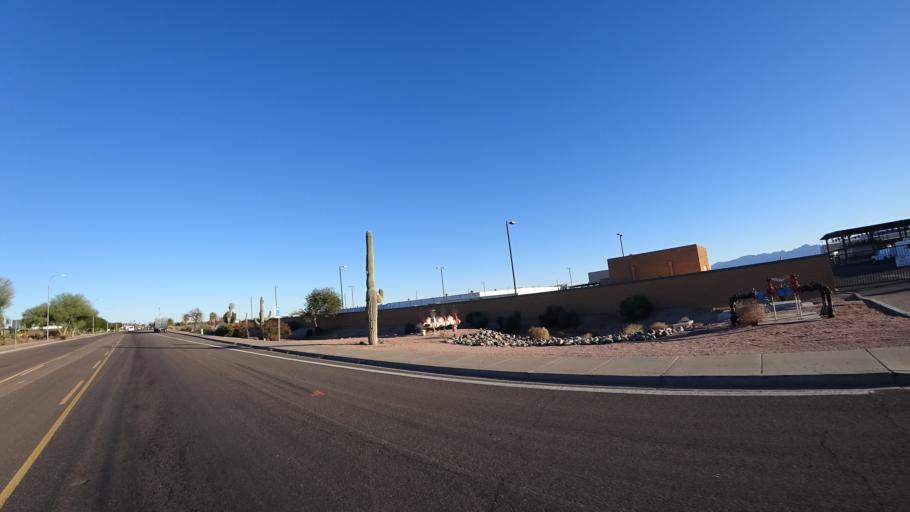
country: US
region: Arizona
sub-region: Maricopa County
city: Tolleson
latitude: 33.4517
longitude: -112.2272
